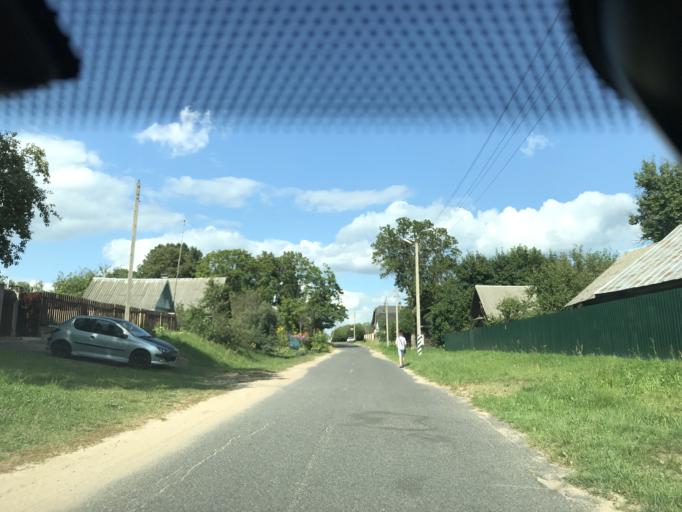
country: BY
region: Mogilev
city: Poselok Voskhod
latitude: 53.7892
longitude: 30.3584
